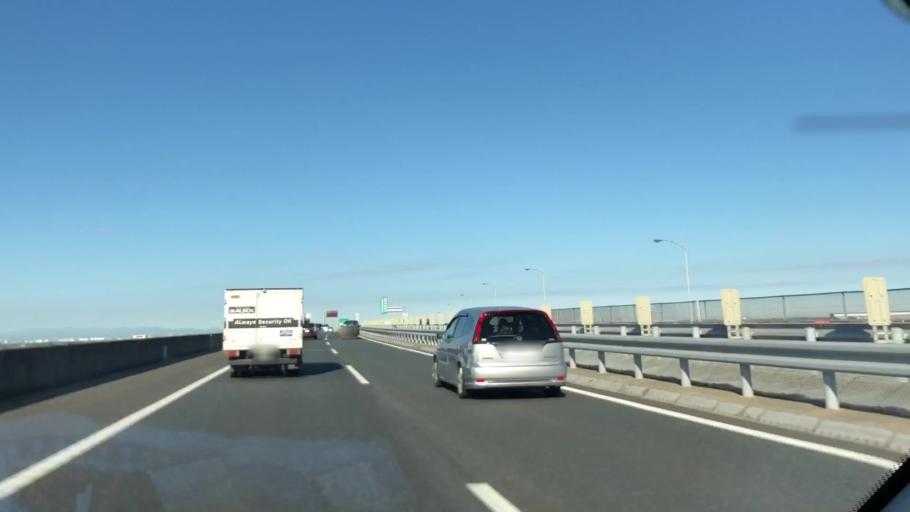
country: JP
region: Chiba
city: Kisarazu
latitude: 35.4238
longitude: 139.9333
